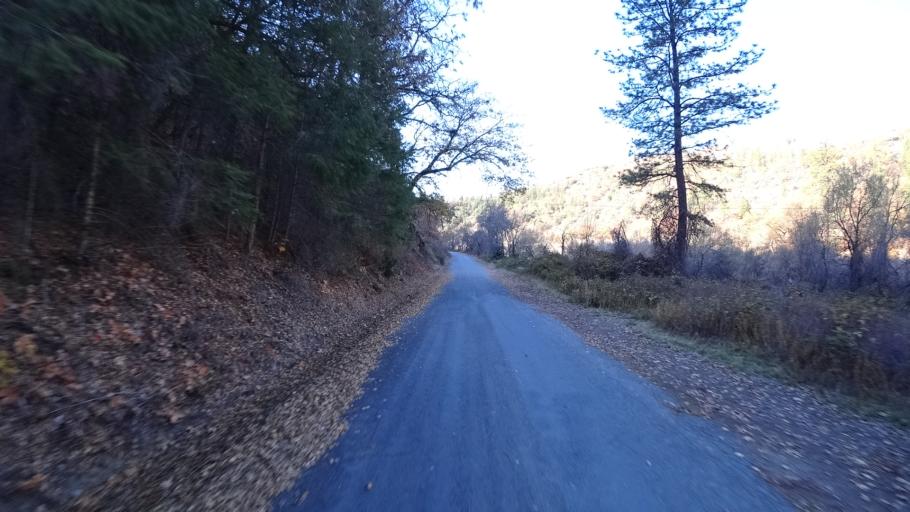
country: US
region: California
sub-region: Siskiyou County
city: Yreka
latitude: 41.8295
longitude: -122.9581
